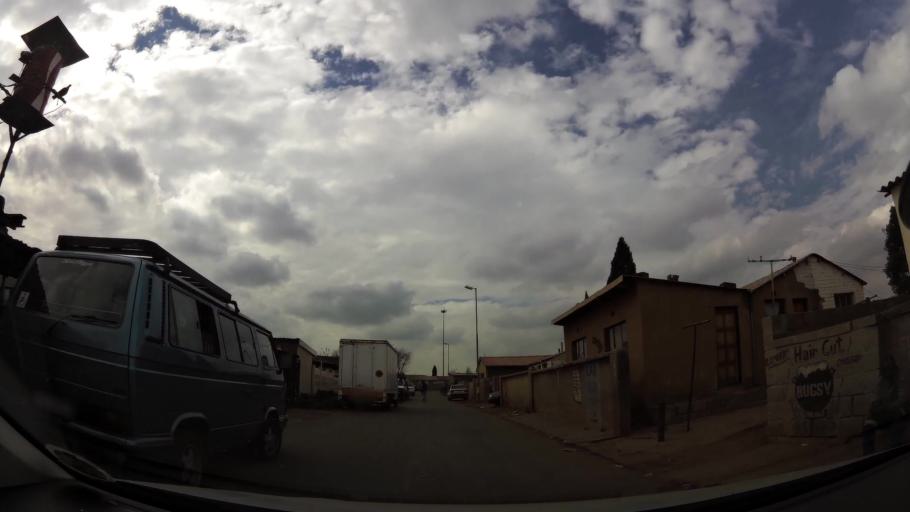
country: ZA
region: Gauteng
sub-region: City of Johannesburg Metropolitan Municipality
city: Soweto
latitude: -26.2700
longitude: 27.8514
